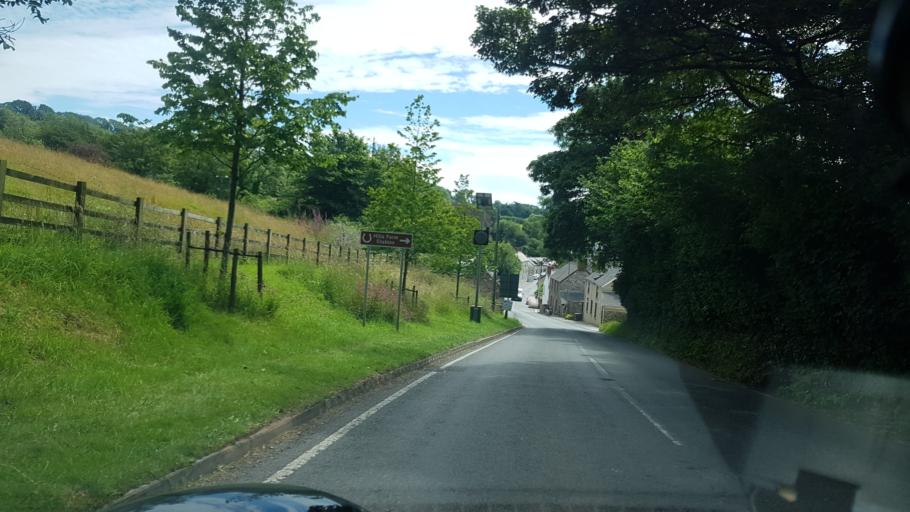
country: GB
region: Wales
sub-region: Carmarthenshire
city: Saint Clears
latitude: 51.7762
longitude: -4.4649
